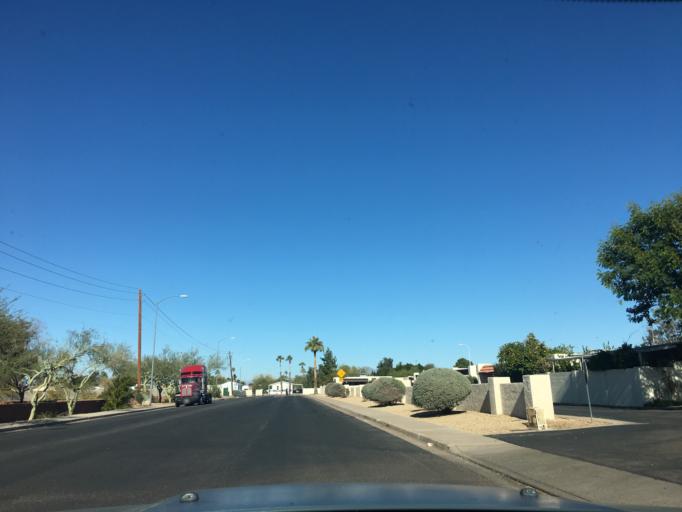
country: US
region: Arizona
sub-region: Maricopa County
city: Mesa
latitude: 33.4466
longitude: -111.8439
